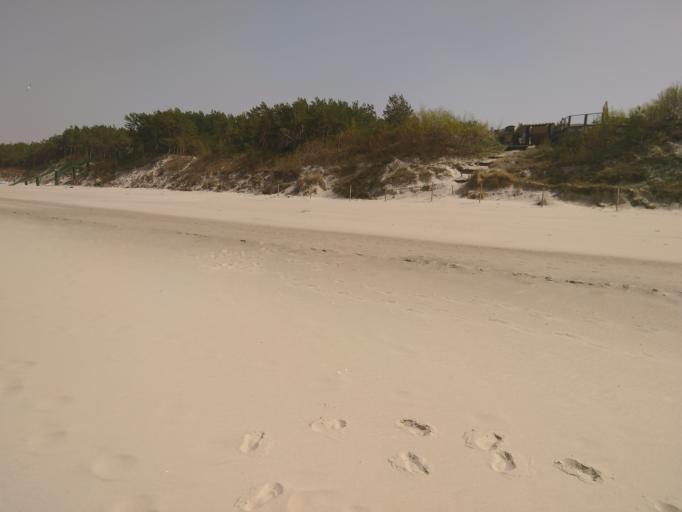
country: PL
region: West Pomeranian Voivodeship
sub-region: Powiat kamienski
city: Dziwnow
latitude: 54.0106
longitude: 14.6934
